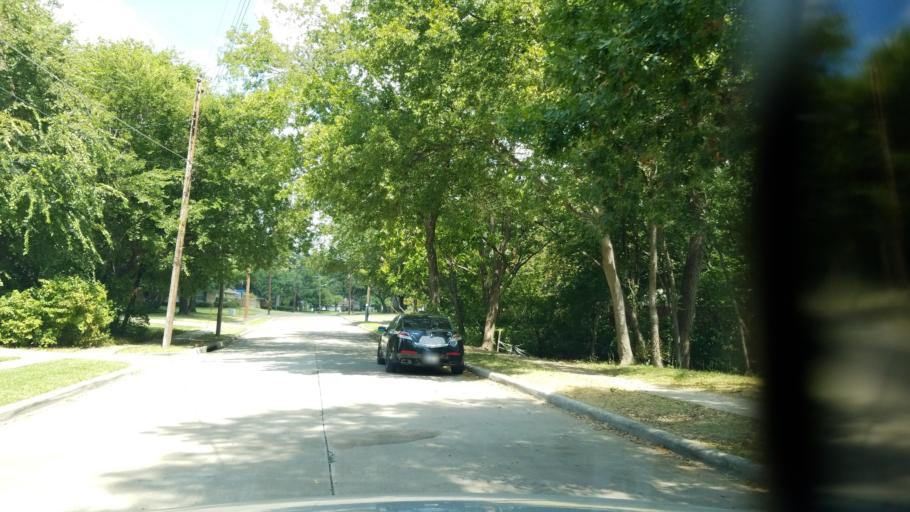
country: US
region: Texas
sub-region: Dallas County
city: Richardson
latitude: 32.9651
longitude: -96.7580
